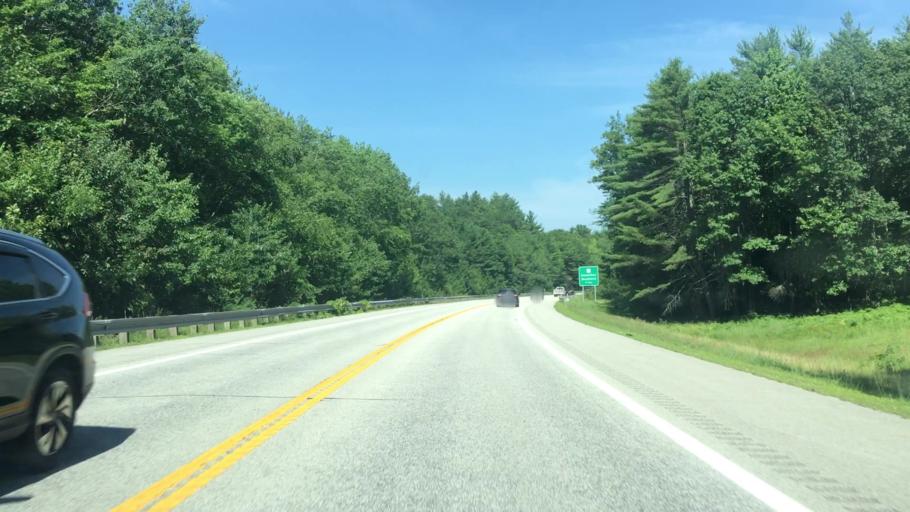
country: US
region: New Hampshire
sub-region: Merrimack County
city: Henniker
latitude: 43.1856
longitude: -71.8017
